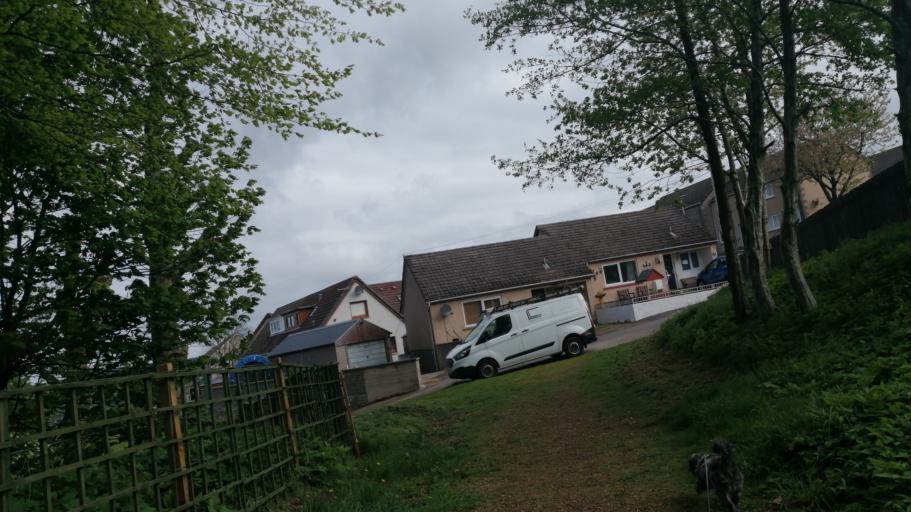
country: GB
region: Scotland
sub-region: Moray
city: Keith
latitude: 57.5381
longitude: -2.9585
